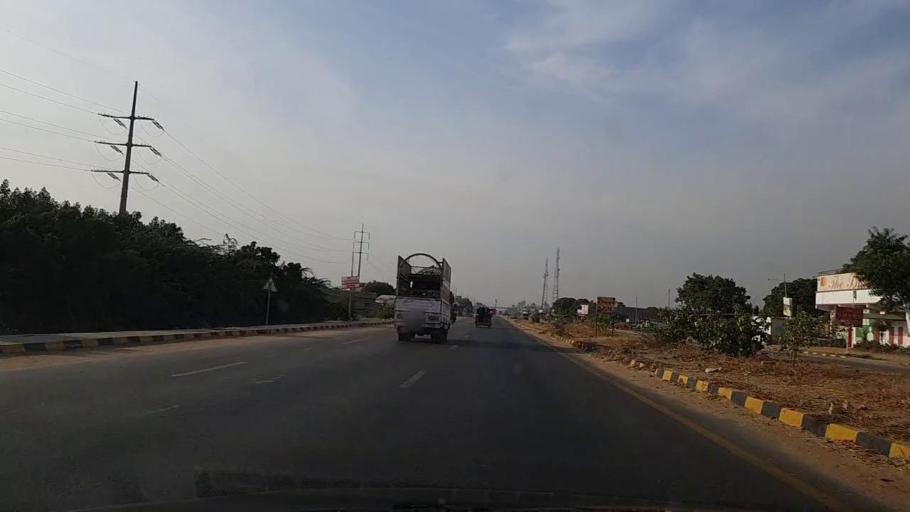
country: PK
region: Sindh
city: Gharo
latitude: 24.7854
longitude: 67.5313
